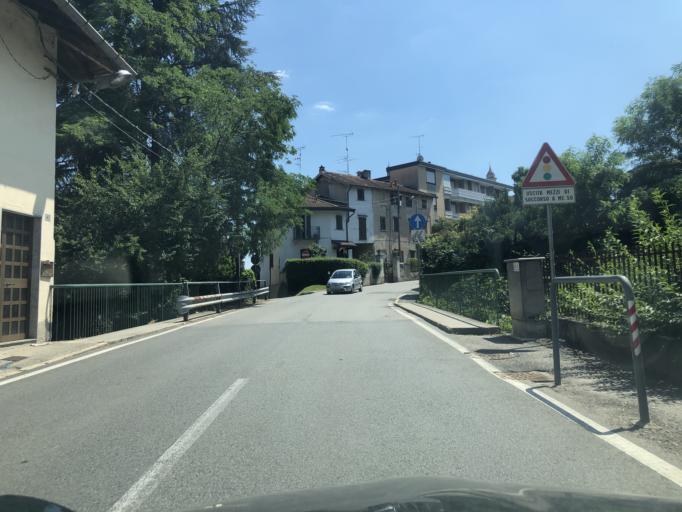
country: IT
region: Piedmont
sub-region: Provincia di Novara
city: Arona
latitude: 45.7514
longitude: 8.5485
